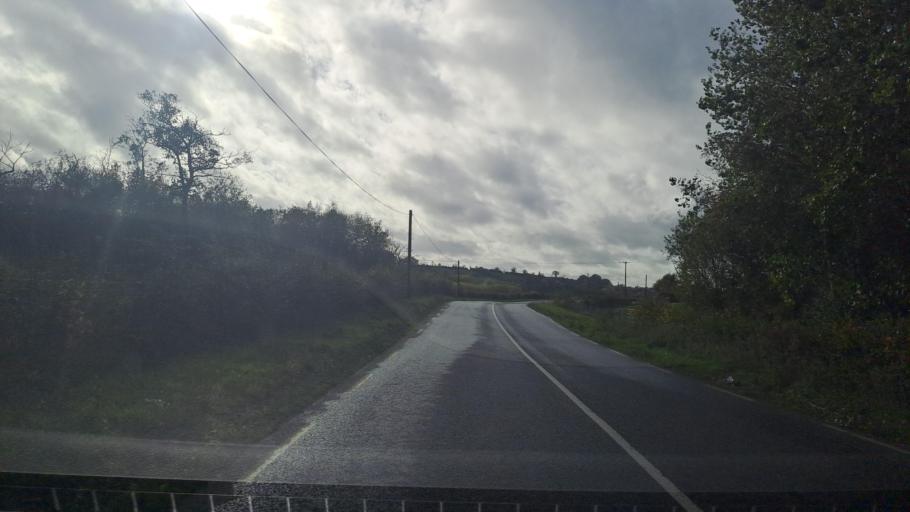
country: IE
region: Ulster
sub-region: County Monaghan
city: Monaghan
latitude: 54.1121
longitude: -6.9477
